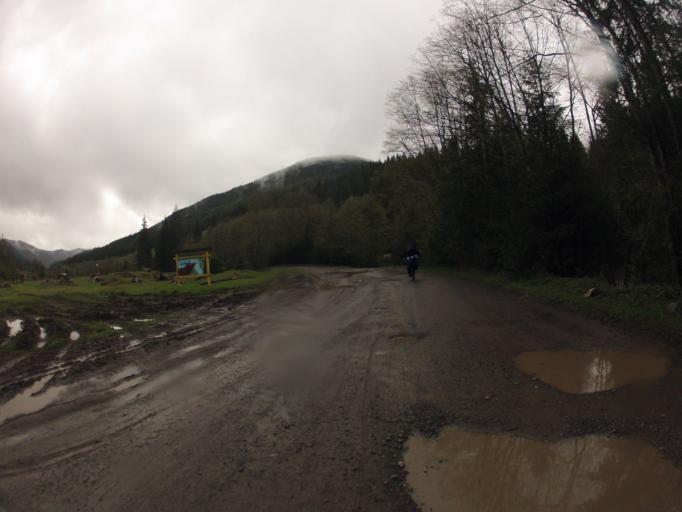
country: RO
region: Suceava
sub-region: Comuna Izvoarele Sucevei
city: Izvoarele Sucevei
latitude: 47.8331
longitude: 25.0566
